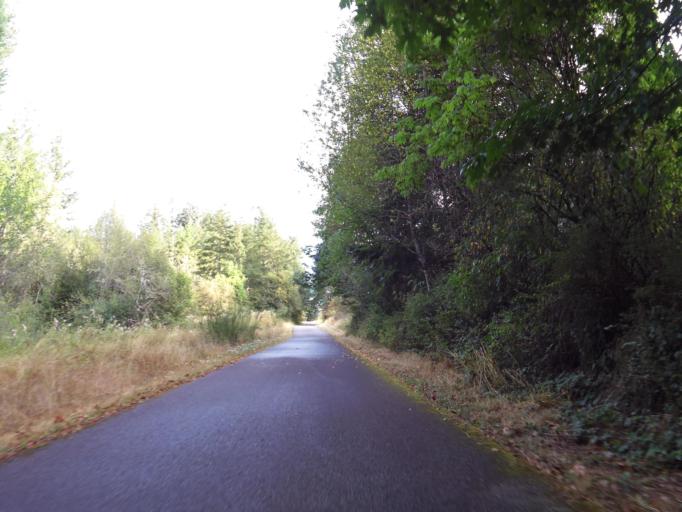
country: US
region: Washington
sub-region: Thurston County
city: Tenino
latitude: 46.9185
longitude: -122.8004
